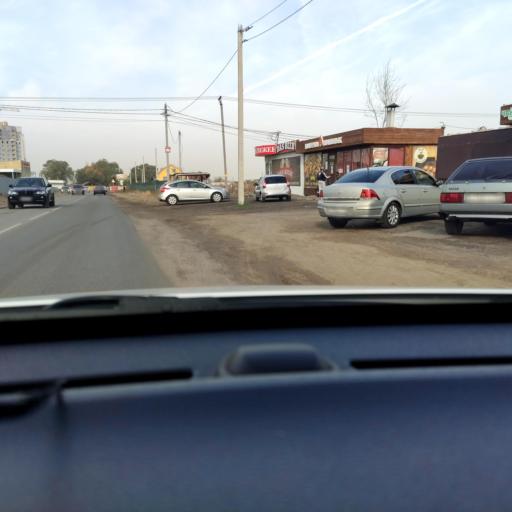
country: RU
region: Voronezj
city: Podgornoye
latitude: 51.7208
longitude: 39.1483
